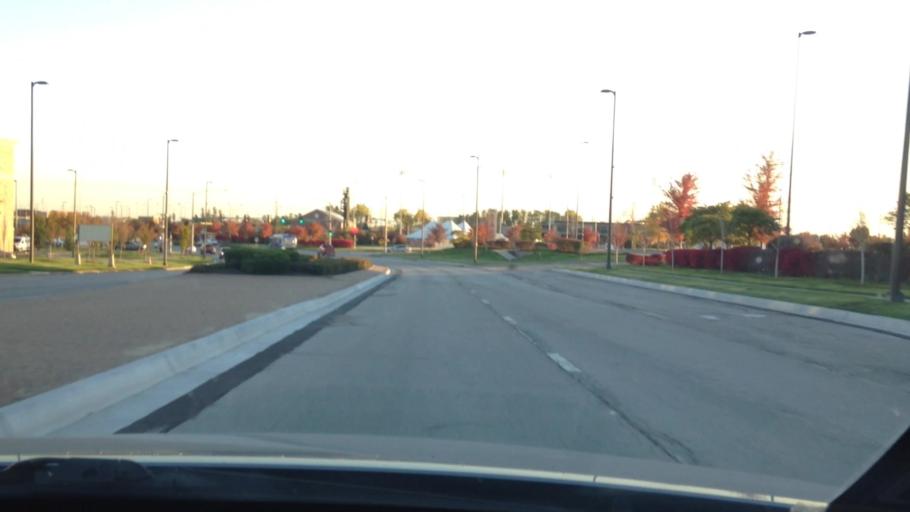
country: US
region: Kansas
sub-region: Wyandotte County
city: Edwardsville
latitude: 39.1279
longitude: -94.8302
